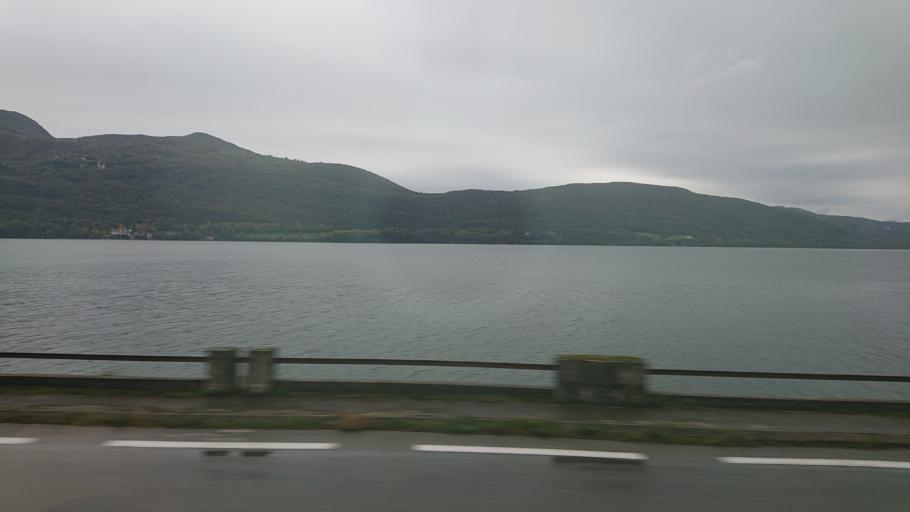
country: FR
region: Rhone-Alpes
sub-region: Departement de la Savoie
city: Chatillon
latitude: 45.7639
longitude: 5.8704
